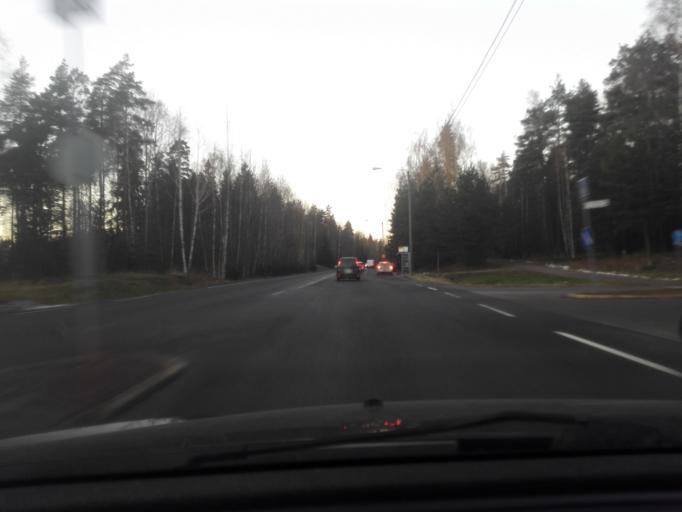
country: FI
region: Uusimaa
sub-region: Helsinki
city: Vantaa
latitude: 60.2877
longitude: 25.1018
